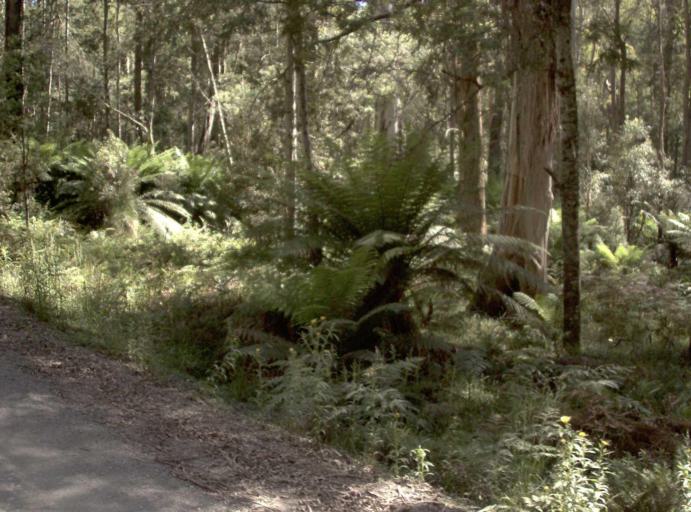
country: AU
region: New South Wales
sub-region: Bombala
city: Bombala
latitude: -37.2329
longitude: 148.7538
